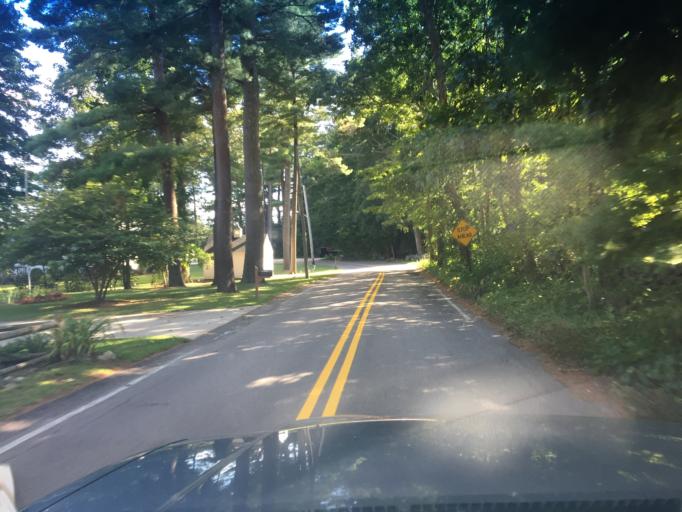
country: US
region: Massachusetts
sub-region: Norfolk County
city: Millis
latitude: 42.1854
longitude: -71.3720
